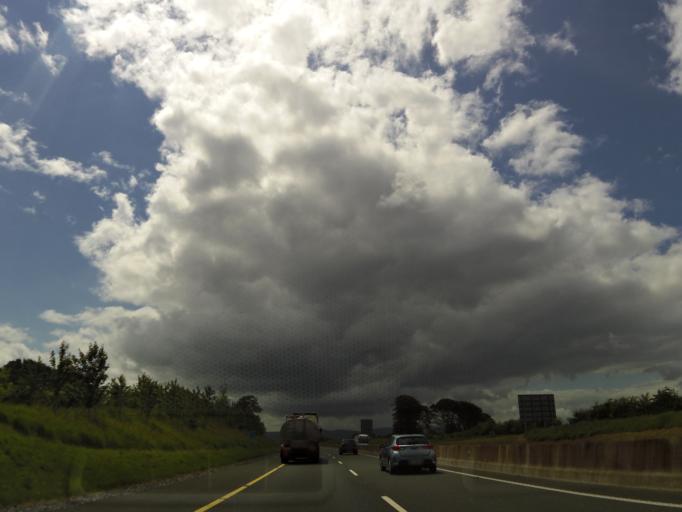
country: IE
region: Munster
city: Cashel
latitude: 52.4892
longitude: -7.9004
